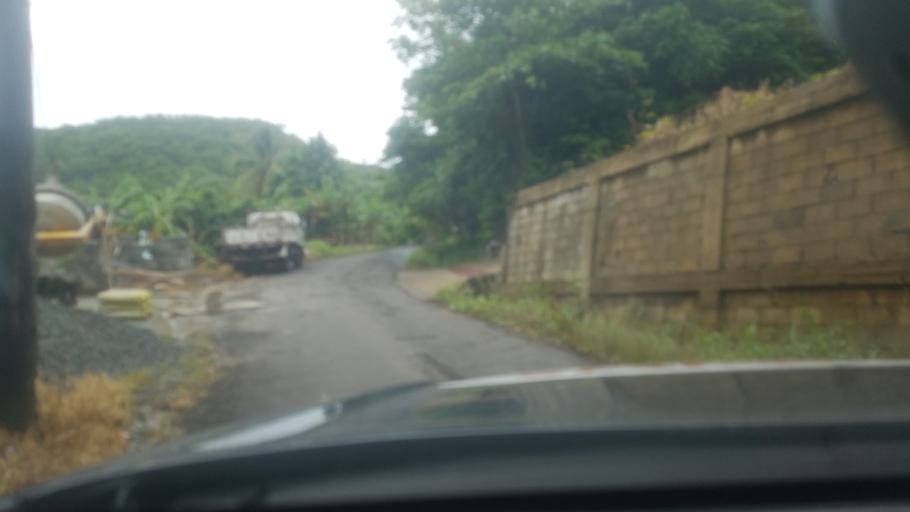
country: LC
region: Gros-Islet
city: Gros Islet
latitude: 14.0448
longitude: -60.9226
